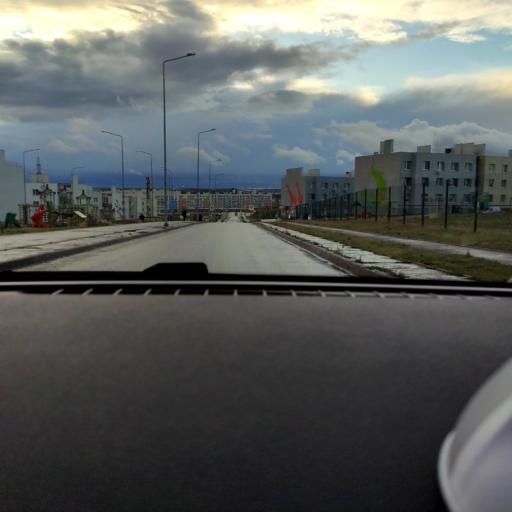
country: RU
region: Samara
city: Petra-Dubrava
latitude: 53.3036
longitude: 50.3431
